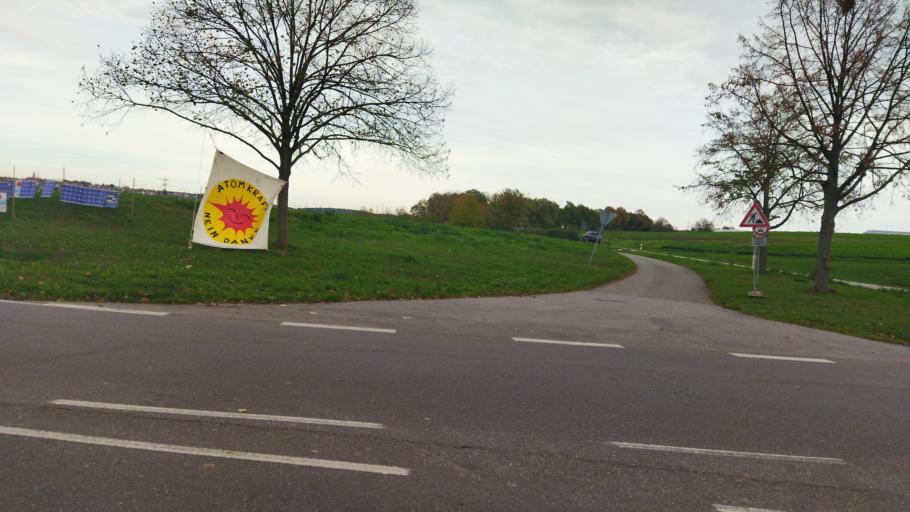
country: DE
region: Baden-Wuerttemberg
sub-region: Regierungsbezirk Stuttgart
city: Gemmrigheim
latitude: 49.0357
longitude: 9.1627
